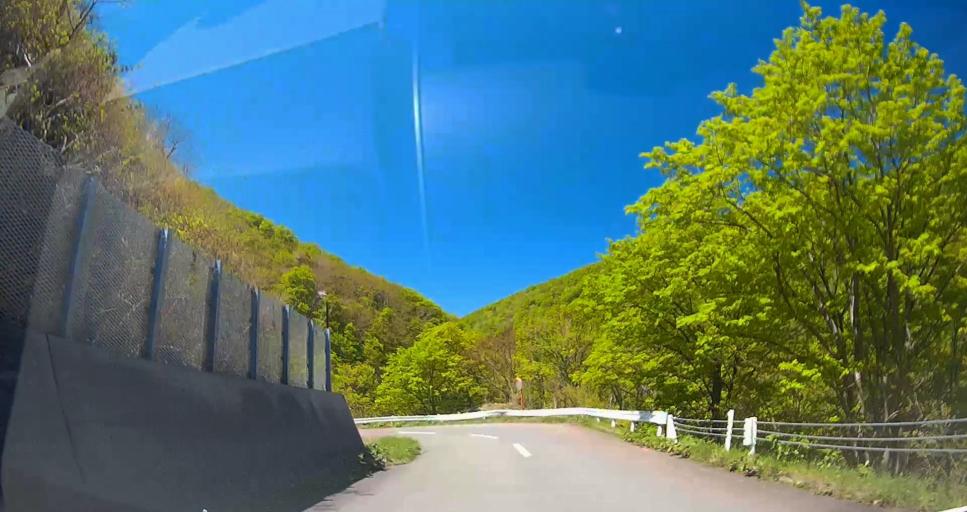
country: JP
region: Aomori
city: Mutsu
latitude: 41.3256
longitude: 140.8150
